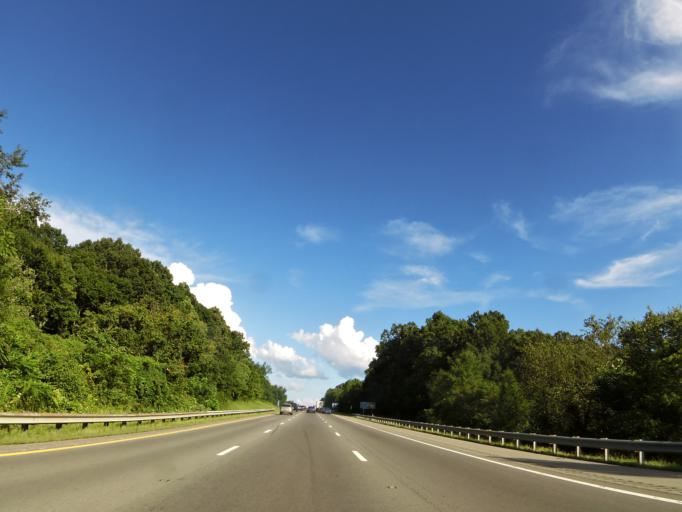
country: US
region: Tennessee
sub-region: Robertson County
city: Coopertown
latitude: 36.3583
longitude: -86.9482
